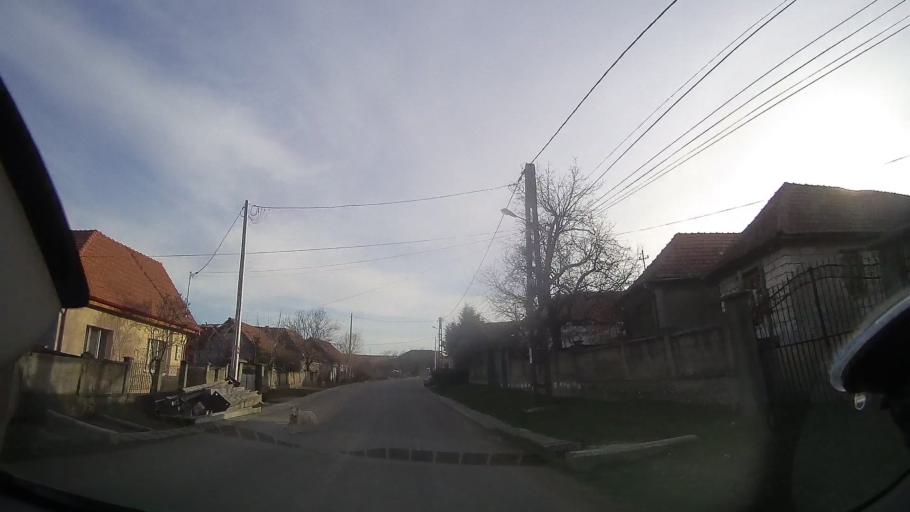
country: RO
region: Bihor
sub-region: Comuna Tileagd
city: Tileagd
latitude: 47.1033
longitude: 22.1747
